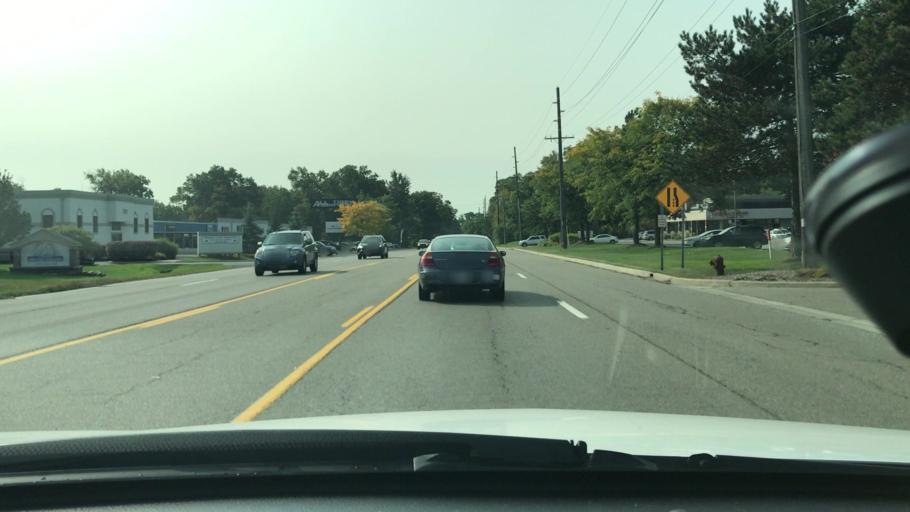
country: US
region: Michigan
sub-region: Oakland County
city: Wolverine Lake
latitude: 42.5911
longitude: -83.4459
